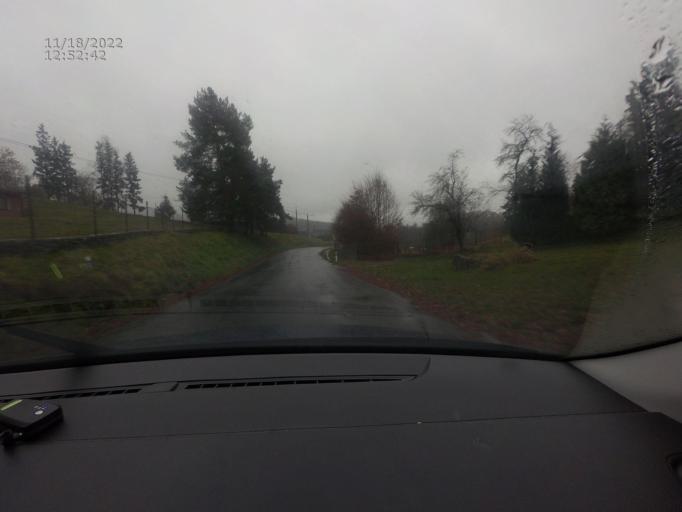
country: CZ
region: Plzensky
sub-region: Okres Klatovy
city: Kolinec
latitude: 49.3279
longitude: 13.4430
